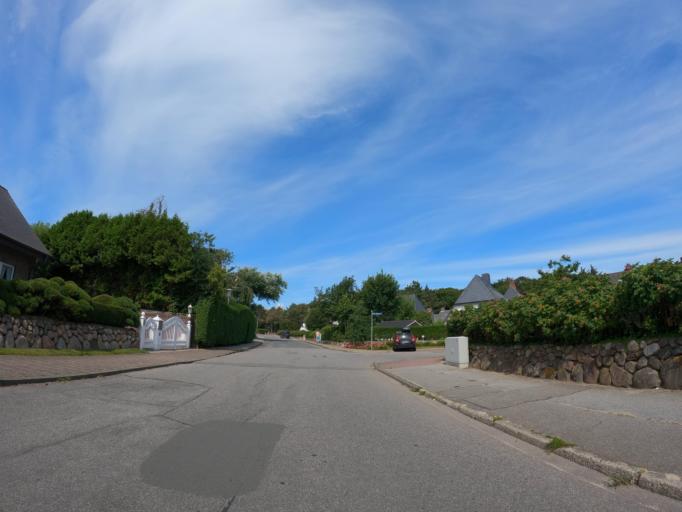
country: DE
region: Schleswig-Holstein
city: Westerland
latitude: 54.9197
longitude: 8.3145
